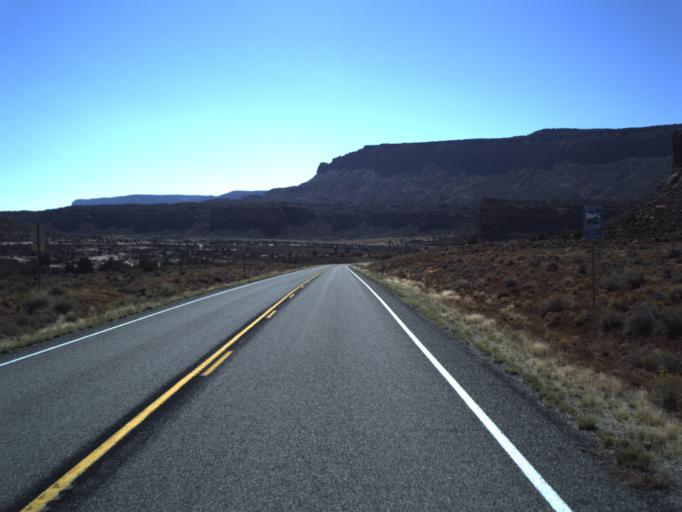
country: US
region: Utah
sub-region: San Juan County
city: Blanding
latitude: 37.7565
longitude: -110.2818
